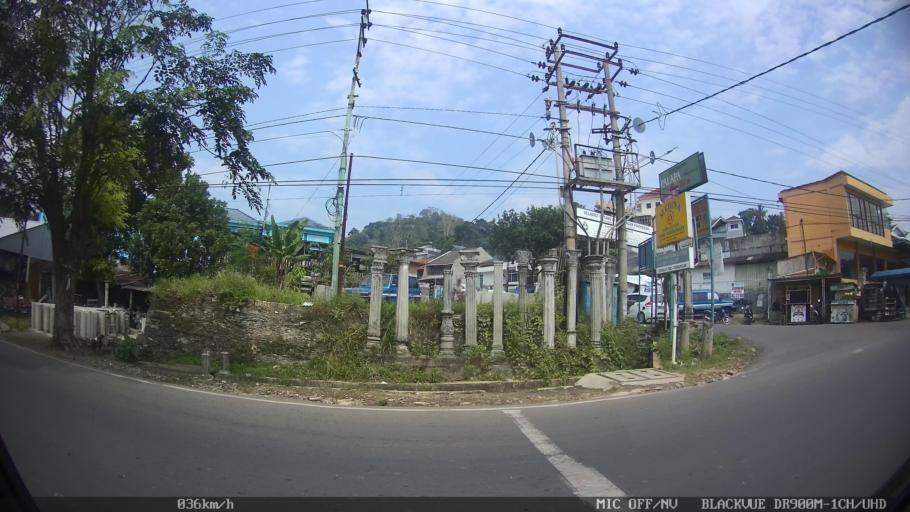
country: ID
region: Lampung
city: Bandarlampung
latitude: -5.4177
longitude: 105.2469
